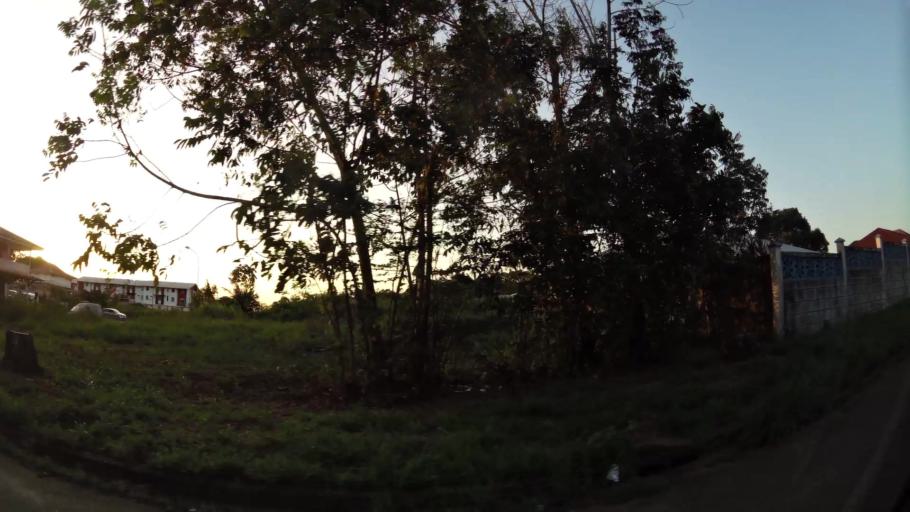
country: GF
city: Macouria
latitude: 4.9292
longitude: -52.4037
